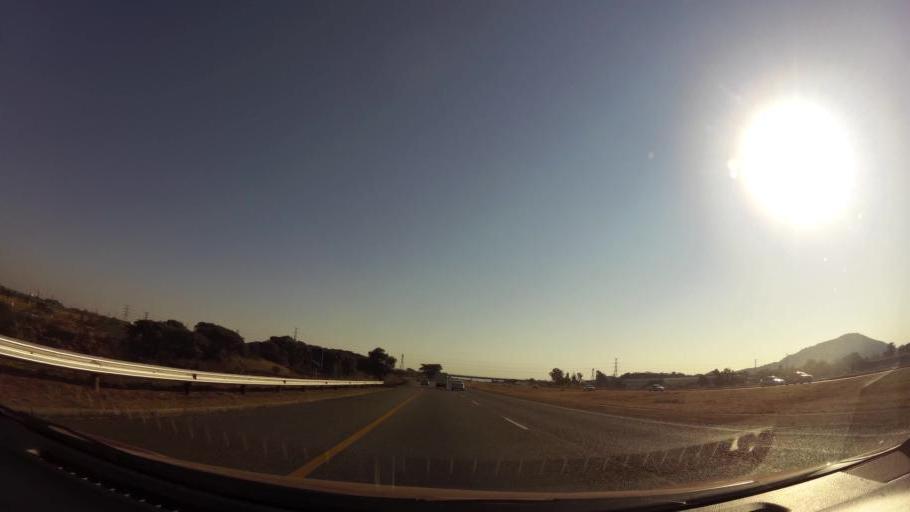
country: ZA
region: North-West
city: Ga-Rankuwa
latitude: -25.6356
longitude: 28.1110
